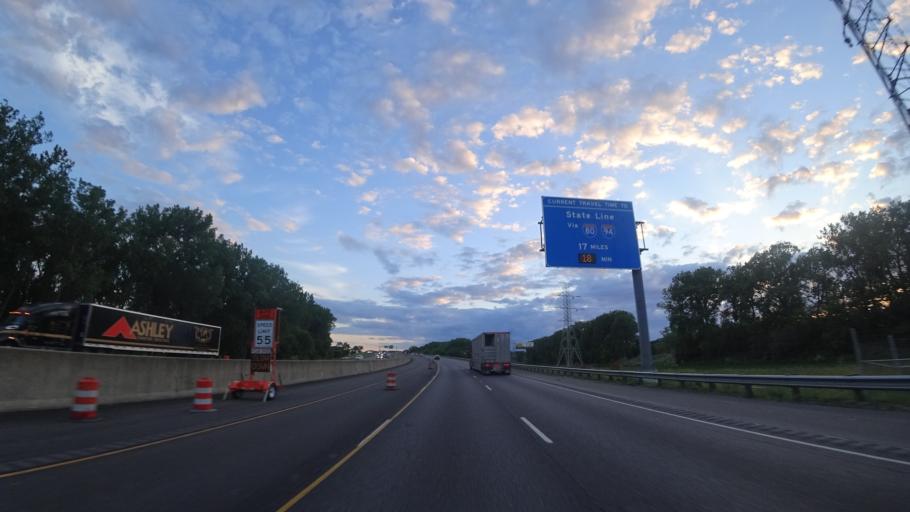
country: US
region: Indiana
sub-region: Porter County
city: Ogden Dunes
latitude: 41.5971
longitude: -87.2106
